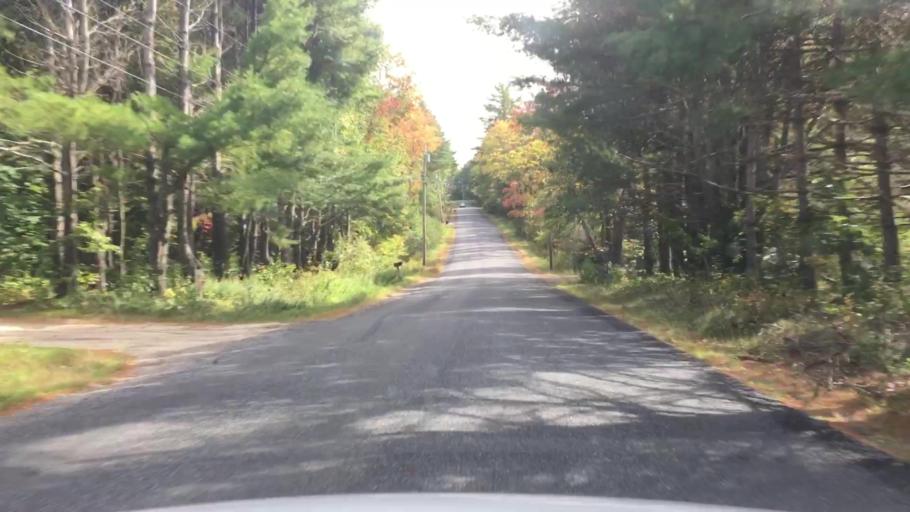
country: US
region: Maine
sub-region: Androscoggin County
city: Lisbon Falls
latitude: 43.9774
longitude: -70.0917
